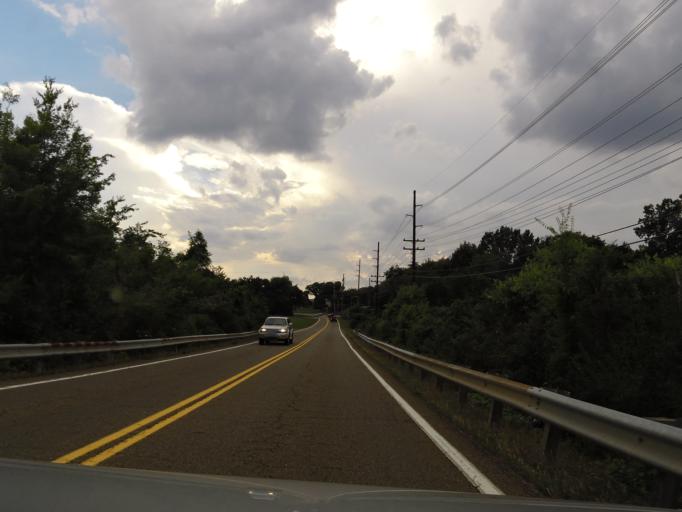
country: US
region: Tennessee
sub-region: Blount County
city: Louisville
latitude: 35.8554
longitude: -84.0867
